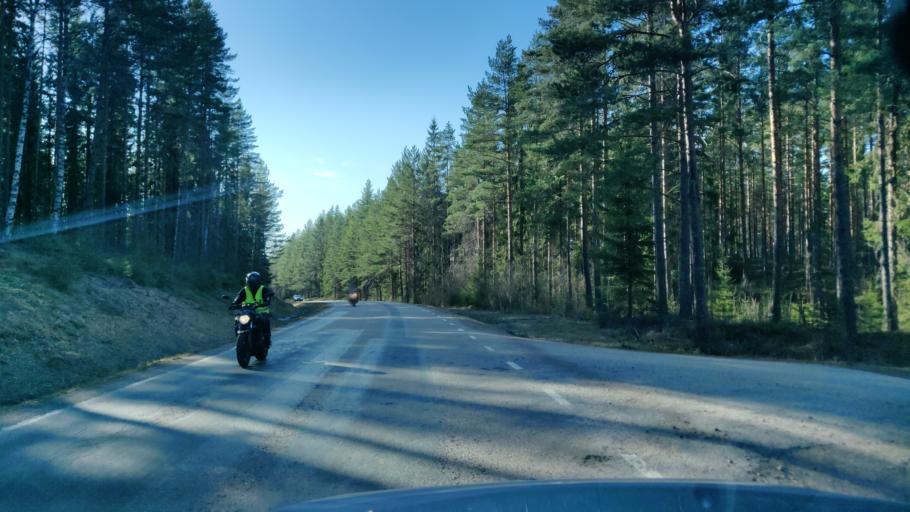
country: SE
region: Vaermland
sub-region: Sunne Kommun
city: Sunne
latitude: 59.9921
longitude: 13.3062
